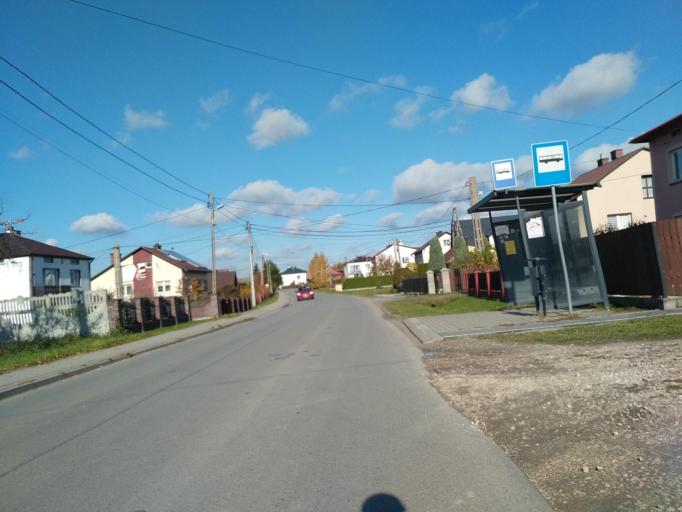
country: PL
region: Subcarpathian Voivodeship
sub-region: Powiat rzeszowski
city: Glogow Malopolski
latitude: 50.1514
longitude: 21.9122
